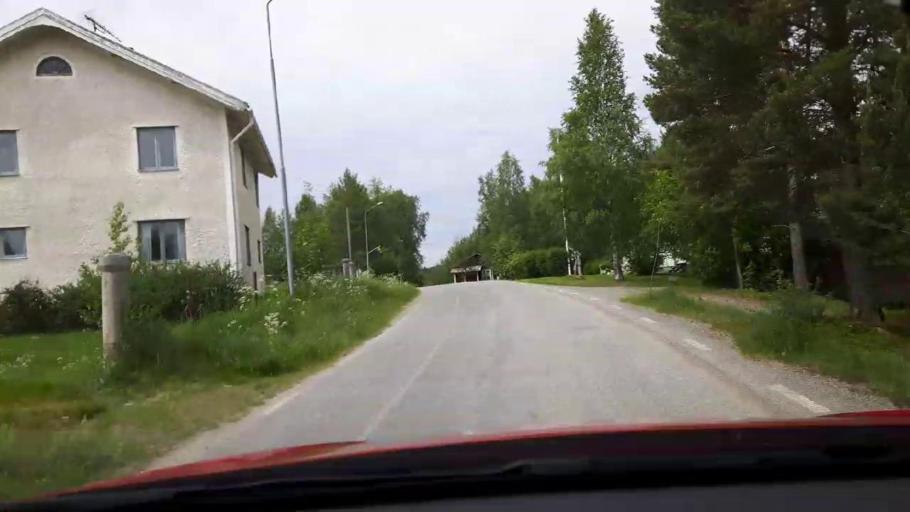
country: SE
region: Jaemtland
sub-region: Harjedalens Kommun
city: Sveg
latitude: 62.4077
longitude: 13.6914
